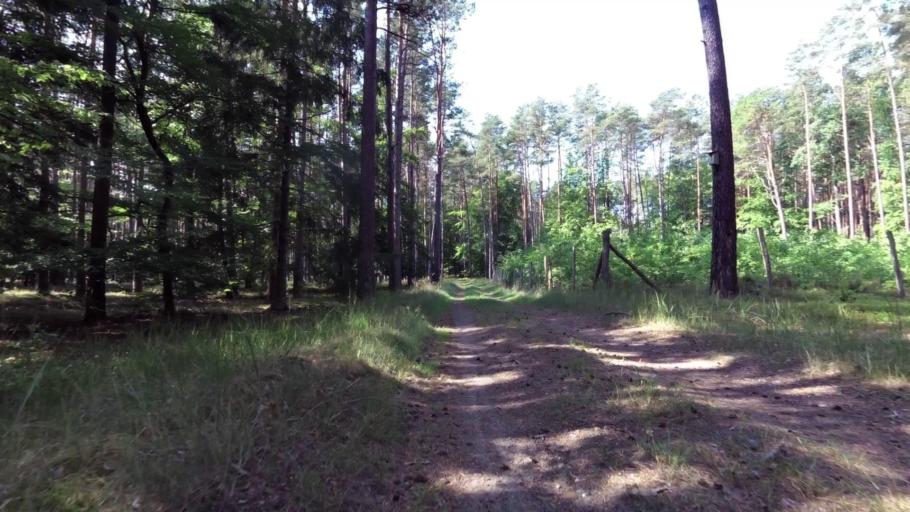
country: PL
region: West Pomeranian Voivodeship
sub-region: Powiat kamienski
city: Miedzyzdroje
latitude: 53.9230
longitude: 14.5049
